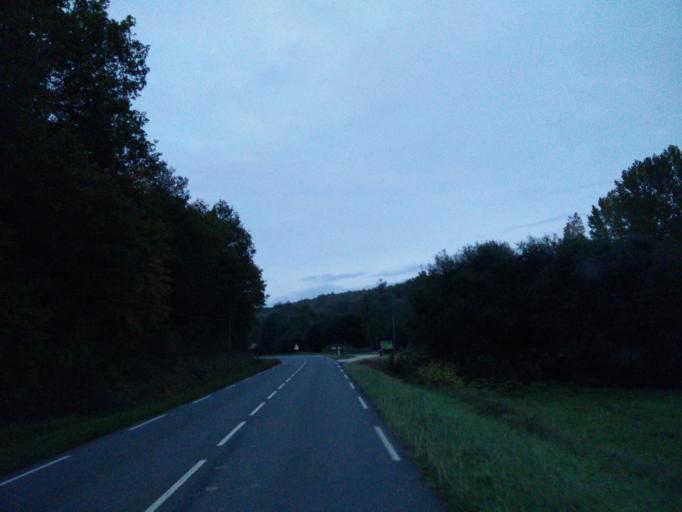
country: FR
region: Aquitaine
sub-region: Departement de la Dordogne
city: Saint-Cyprien
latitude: 44.9111
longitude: 1.1131
